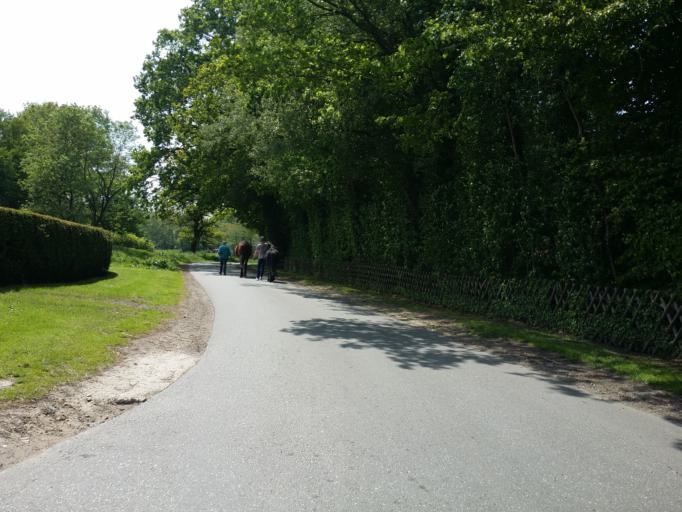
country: DE
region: Lower Saxony
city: Axstedt
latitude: 53.3036
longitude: 8.7531
